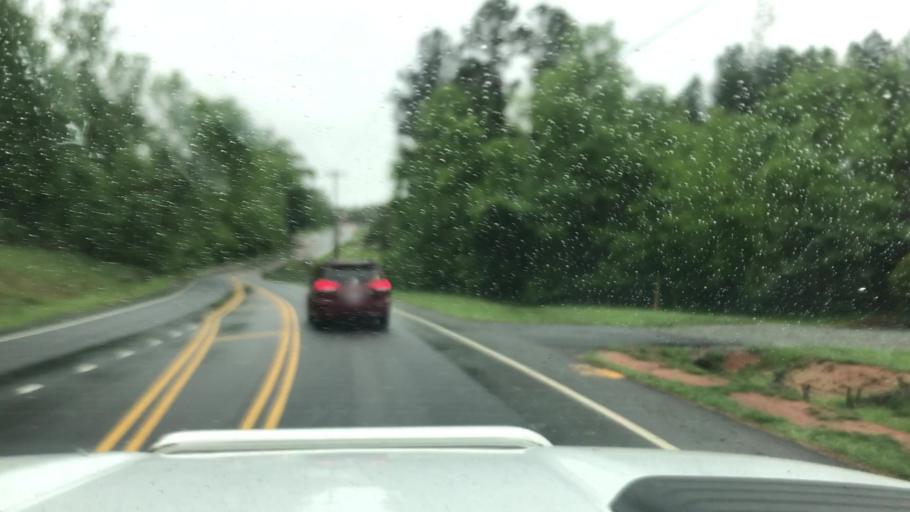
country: US
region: North Carolina
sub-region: Mecklenburg County
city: Huntersville
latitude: 35.4000
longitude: -80.8696
